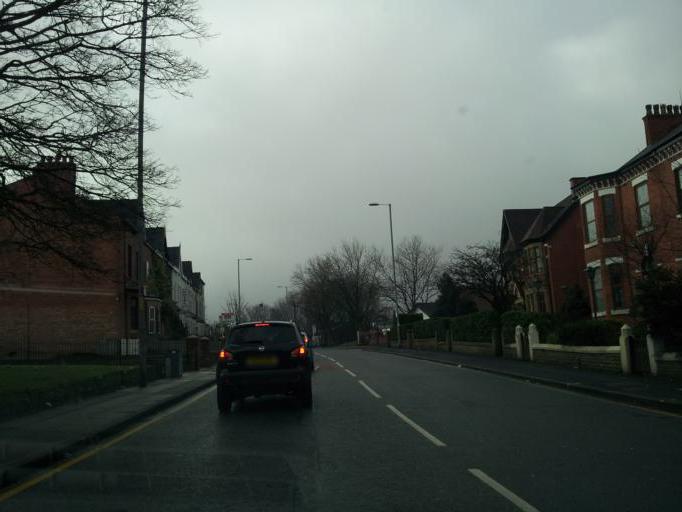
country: GB
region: England
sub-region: Manchester
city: Blackley
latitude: 53.5183
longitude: -2.2132
